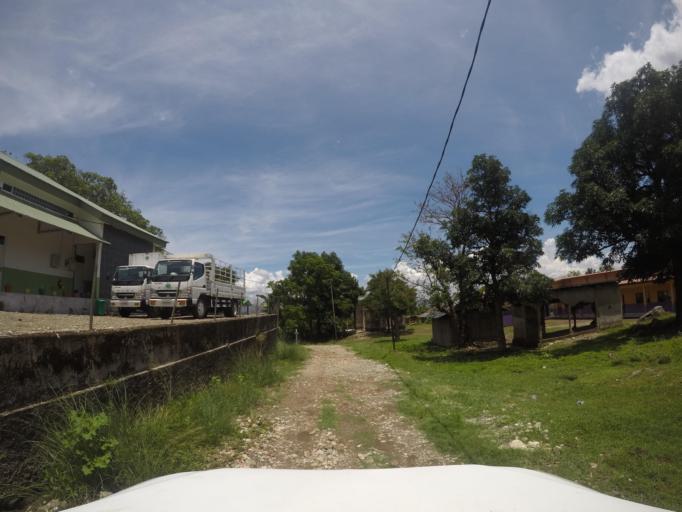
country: TL
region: Bobonaro
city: Maliana
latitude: -8.9976
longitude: 125.2241
